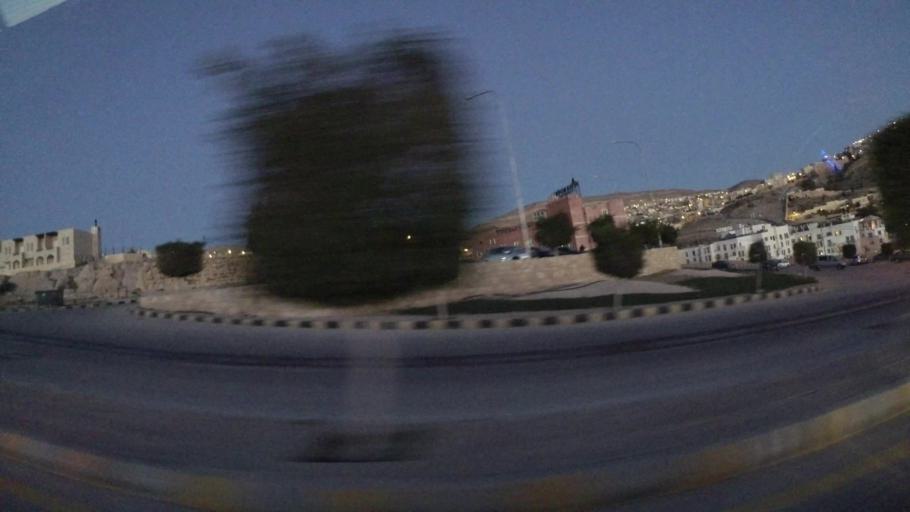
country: JO
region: Ma'an
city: Petra
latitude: 30.3264
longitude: 35.4682
